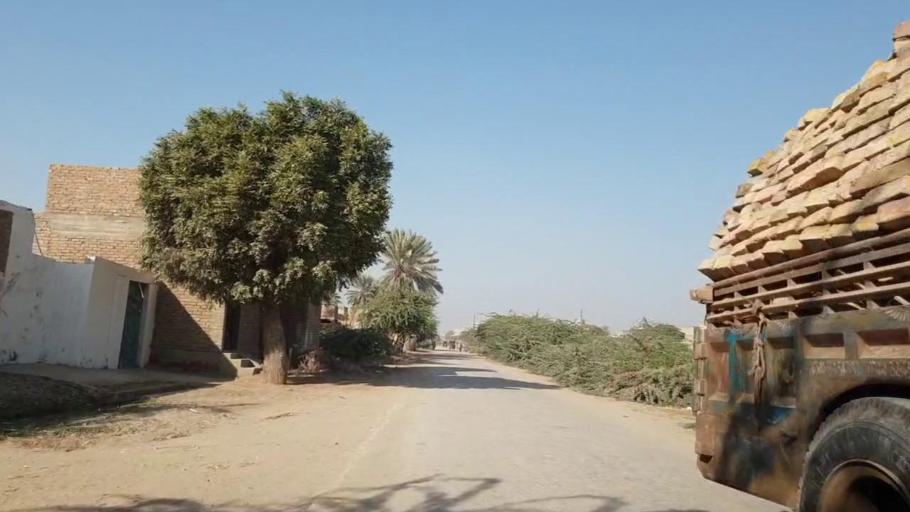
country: PK
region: Sindh
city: Digri
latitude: 25.1478
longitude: 69.1116
